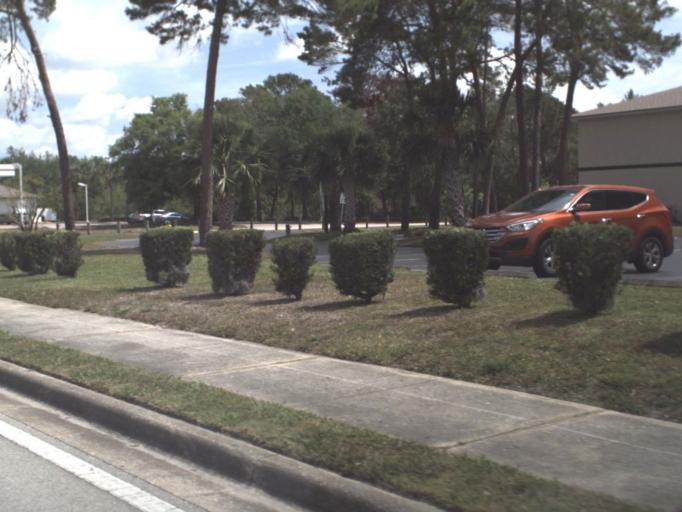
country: US
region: Florida
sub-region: Brevard County
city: Cocoa
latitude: 28.3855
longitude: -80.7550
